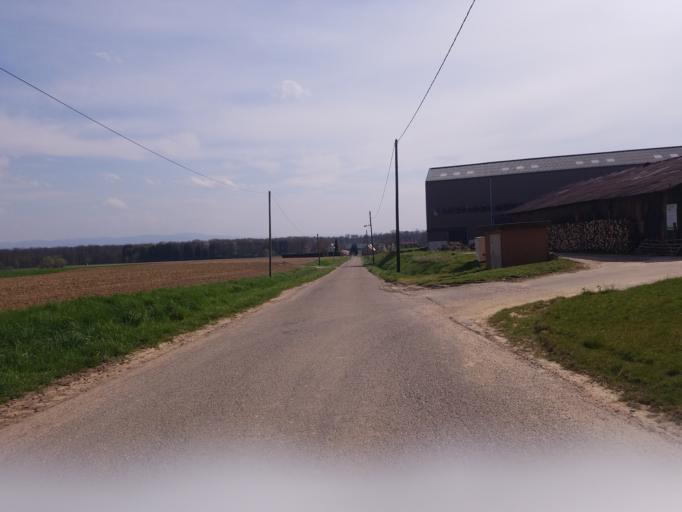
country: FR
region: Alsace
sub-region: Departement du Bas-Rhin
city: Betschdorf
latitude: 48.8989
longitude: 7.9532
